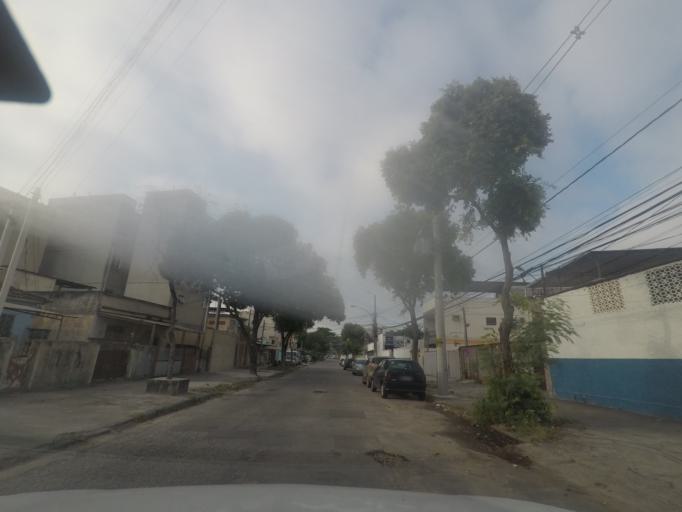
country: BR
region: Rio de Janeiro
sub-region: Duque De Caxias
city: Duque de Caxias
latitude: -22.8336
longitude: -43.2729
